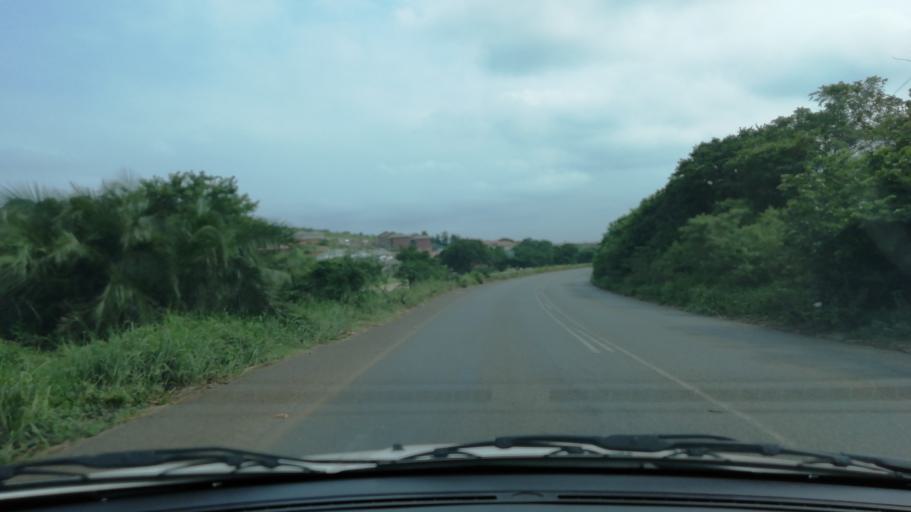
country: ZA
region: KwaZulu-Natal
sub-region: uThungulu District Municipality
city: Empangeni
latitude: -28.7474
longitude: 31.8806
